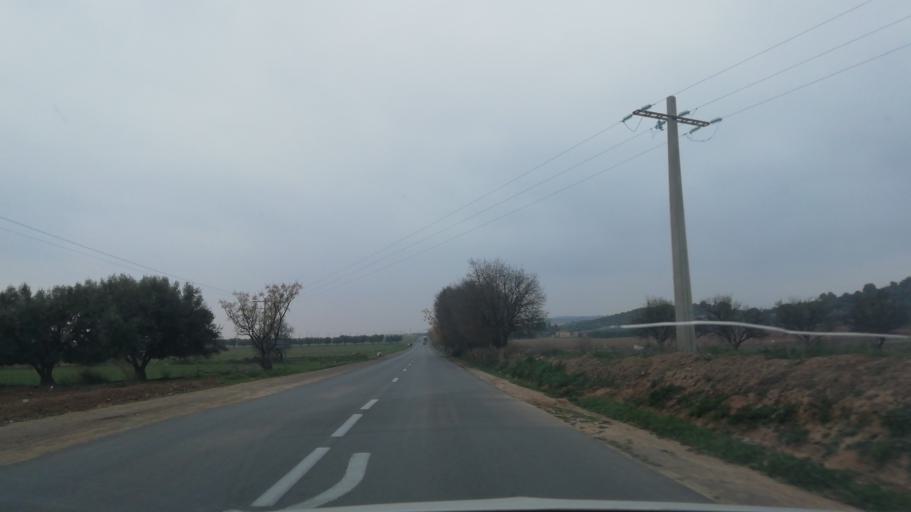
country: DZ
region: Sidi Bel Abbes
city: Sfizef
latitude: 35.2520
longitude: -0.1967
